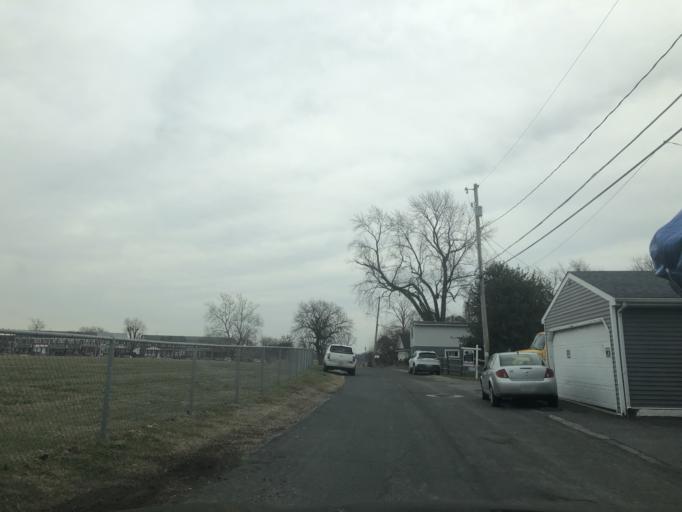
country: US
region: Maryland
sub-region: Baltimore County
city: Dundalk
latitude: 39.2584
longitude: -76.4928
